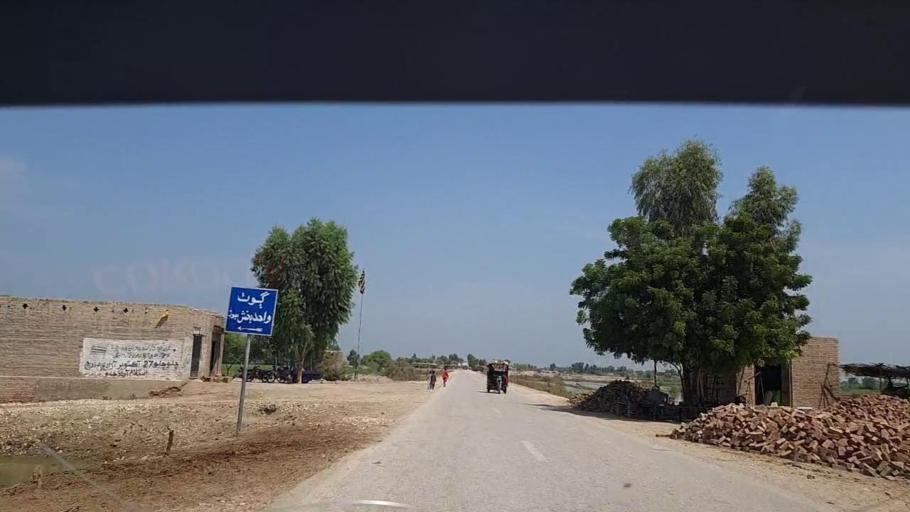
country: PK
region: Sindh
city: Thul
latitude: 28.1133
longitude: 68.8093
